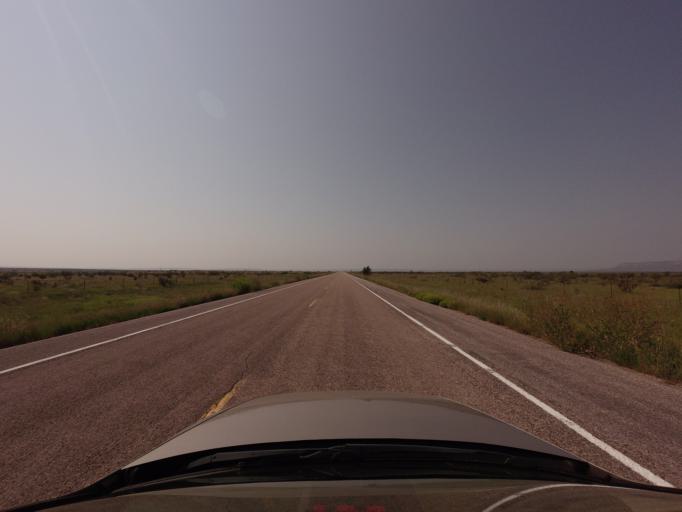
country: US
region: New Mexico
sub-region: Quay County
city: Tucumcari
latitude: 34.9711
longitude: -103.7531
